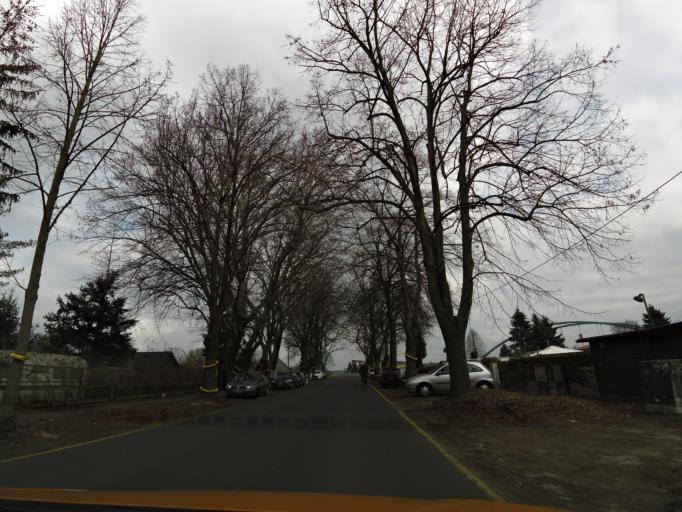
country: DE
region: Brandenburg
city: Werder
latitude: 52.4502
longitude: 12.9785
